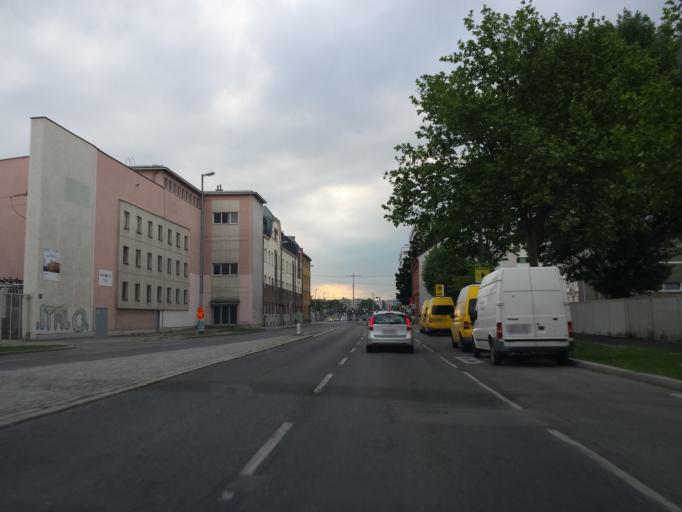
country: AT
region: Lower Austria
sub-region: Politischer Bezirk Wien-Umgebung
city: Gerasdorf bei Wien
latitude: 48.2275
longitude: 16.4599
